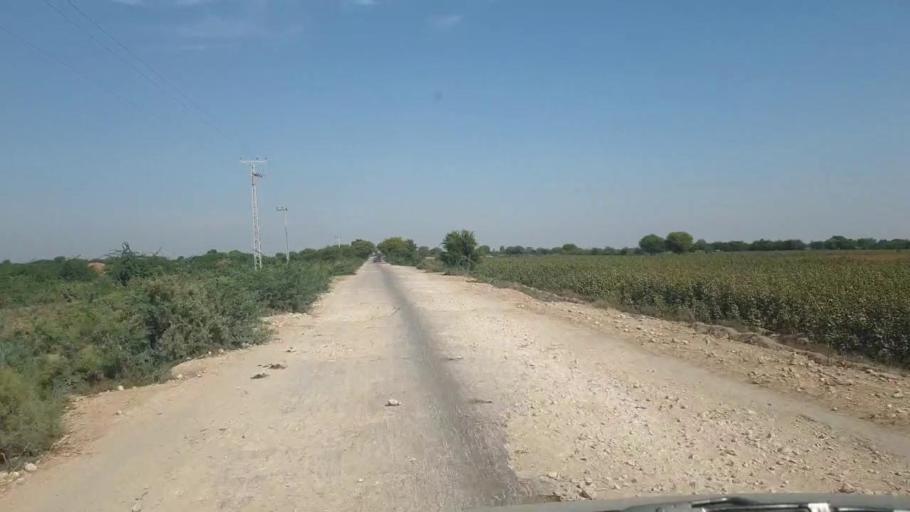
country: PK
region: Sindh
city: Tando Bago
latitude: 24.8715
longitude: 68.9984
